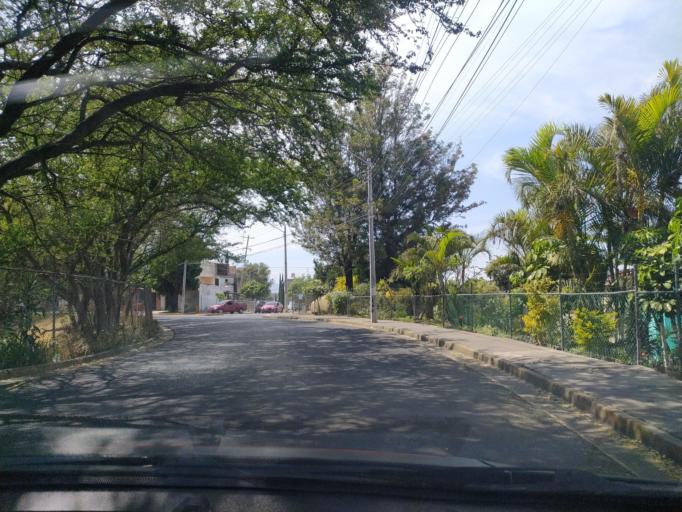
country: MX
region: Jalisco
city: Las Pintas de Arriba
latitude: 20.6188
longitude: -103.3497
